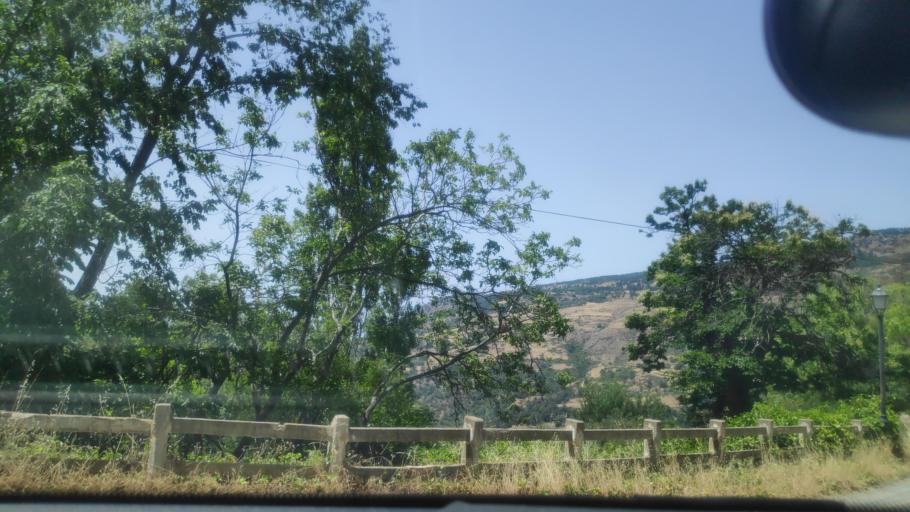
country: ES
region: Andalusia
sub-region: Provincia de Granada
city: Capileira
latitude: 36.9608
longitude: -3.3558
